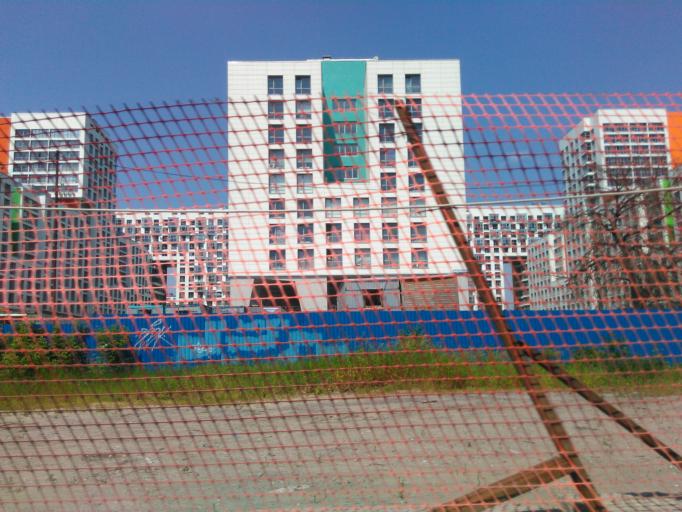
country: RU
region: Moskovskaya
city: Balashikha
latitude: 55.7966
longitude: 37.9632
